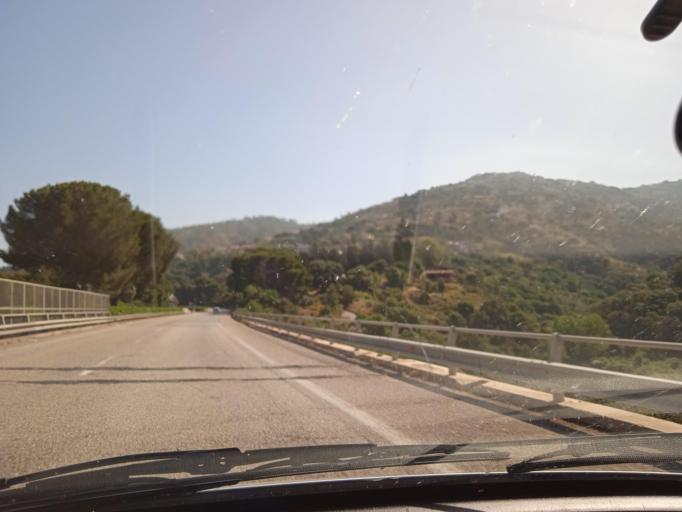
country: IT
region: Sicily
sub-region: Messina
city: Capo d'Orlando
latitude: 38.1287
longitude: 14.7327
